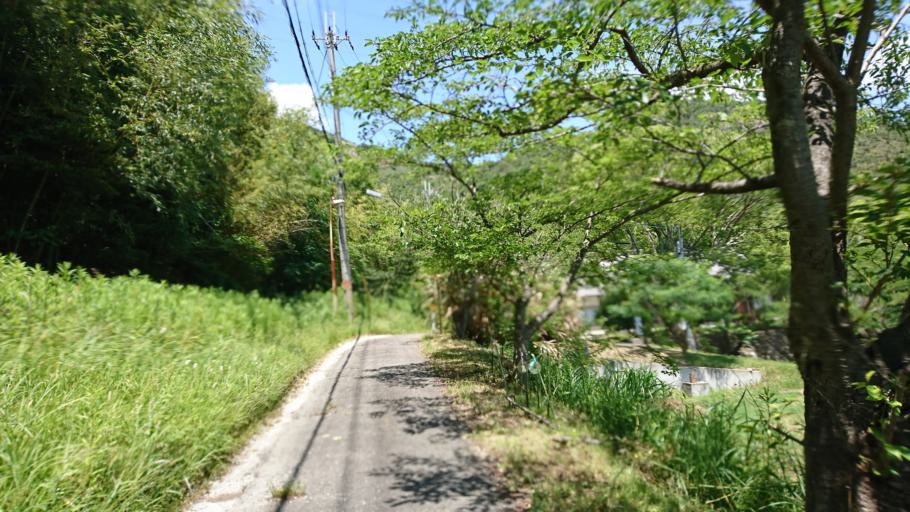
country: JP
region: Hyogo
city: Kakogawacho-honmachi
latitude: 34.8080
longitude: 134.7931
